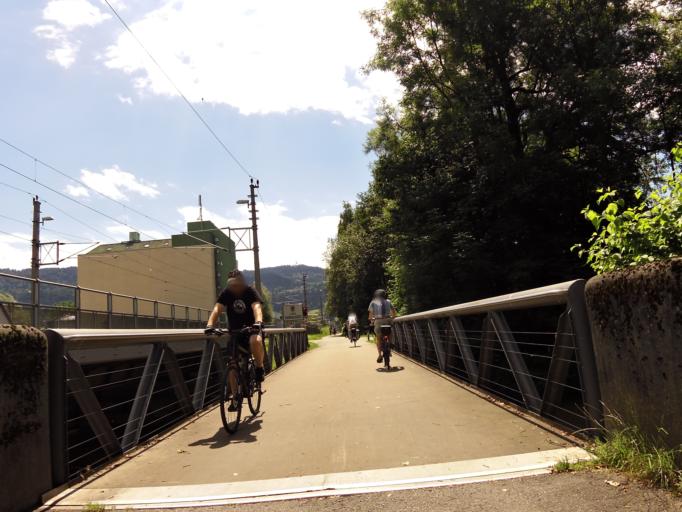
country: AT
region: Vorarlberg
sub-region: Politischer Bezirk Bregenz
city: Lochau
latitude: 47.5344
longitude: 9.7357
